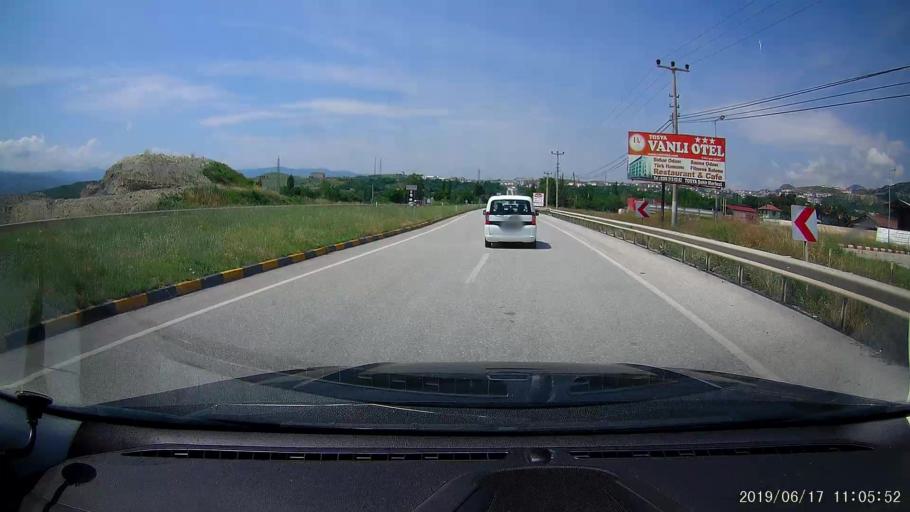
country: TR
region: Kastamonu
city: Tosya
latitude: 41.0177
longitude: 34.0751
